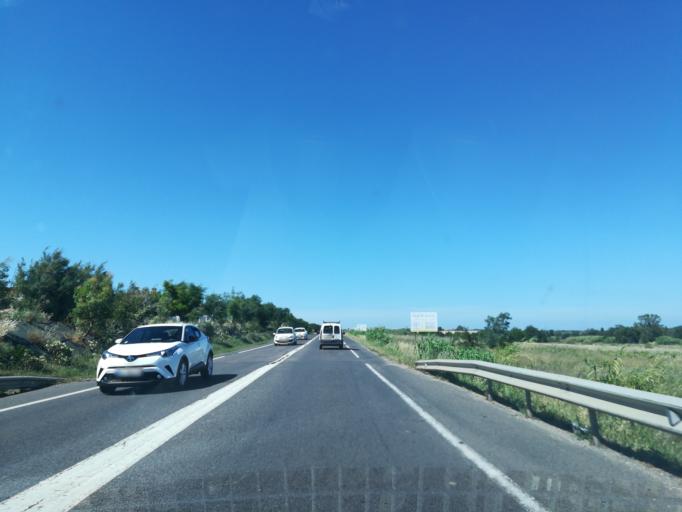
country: FR
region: Languedoc-Roussillon
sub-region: Departement des Pyrenees-Orientales
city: Pollestres
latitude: 42.6322
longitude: 2.8717
